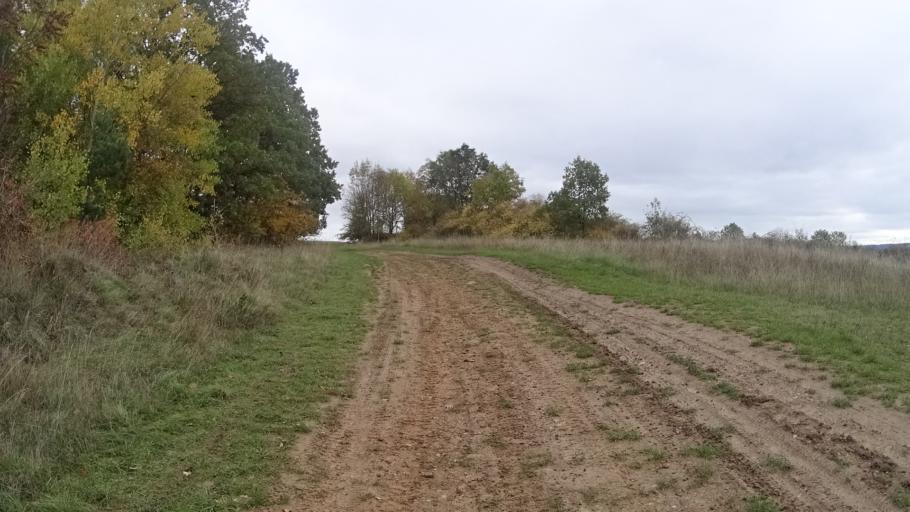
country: DE
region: Thuringia
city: Gossel
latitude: 50.8417
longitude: 10.8862
